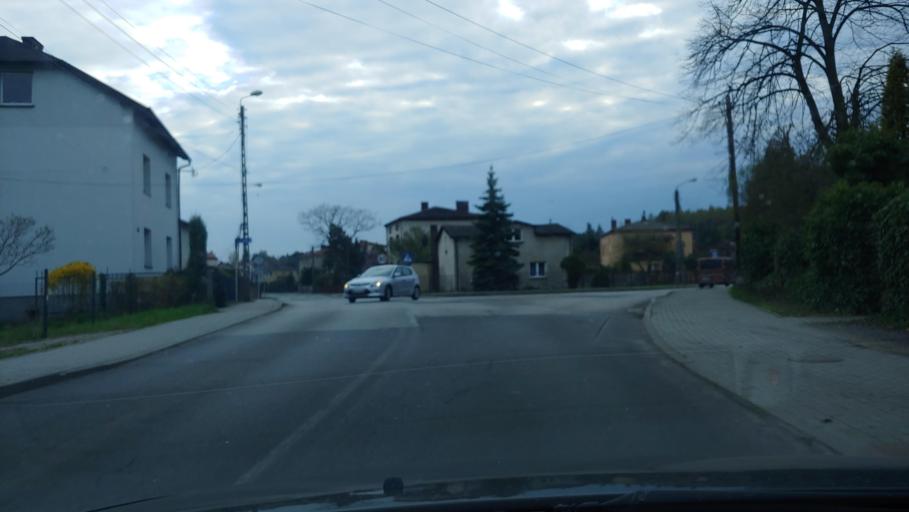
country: PL
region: Silesian Voivodeship
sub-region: Powiat bierunsko-ledzinski
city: Imielin
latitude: 50.1612
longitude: 19.2386
